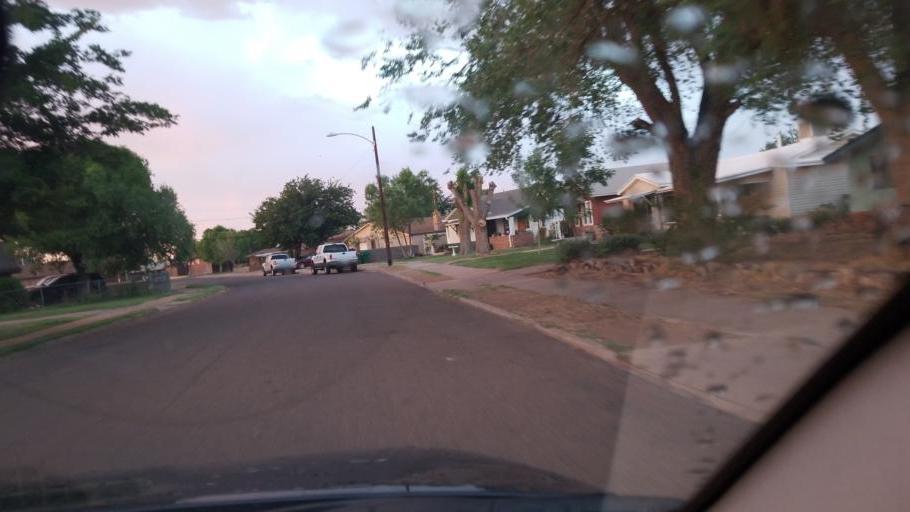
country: US
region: Arizona
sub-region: Navajo County
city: Winslow
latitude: 35.0313
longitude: -110.6948
